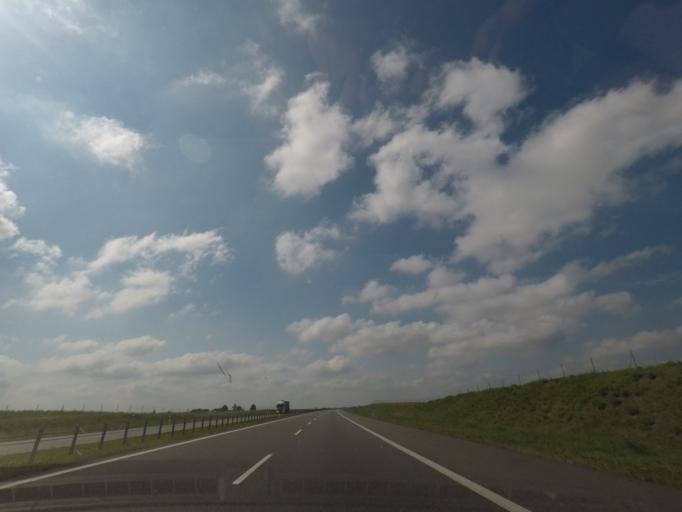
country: PL
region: Kujawsko-Pomorskie
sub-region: Powiat wabrzeski
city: Pluznica
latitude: 53.1974
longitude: 18.7397
